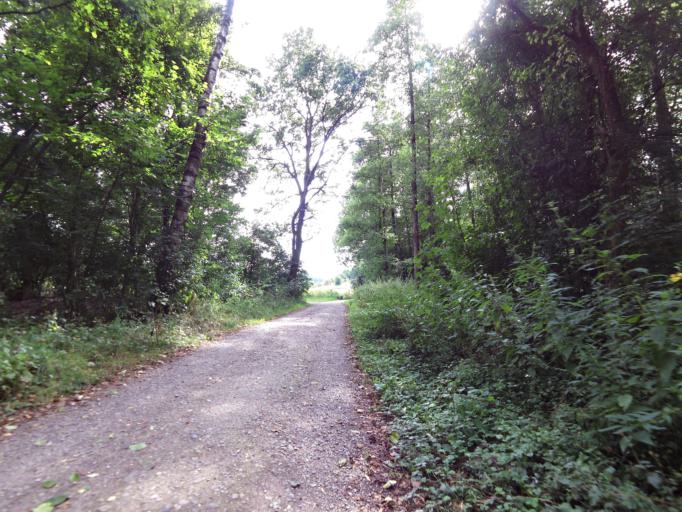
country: CH
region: Zurich
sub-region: Bezirk Dielsdorf
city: Regensdorf
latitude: 47.4353
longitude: 8.4907
